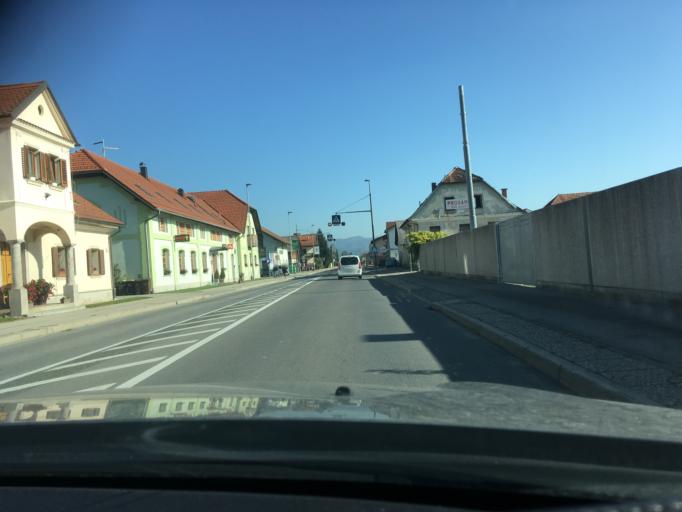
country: SI
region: Domzale
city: Dob
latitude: 46.1528
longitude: 14.6242
